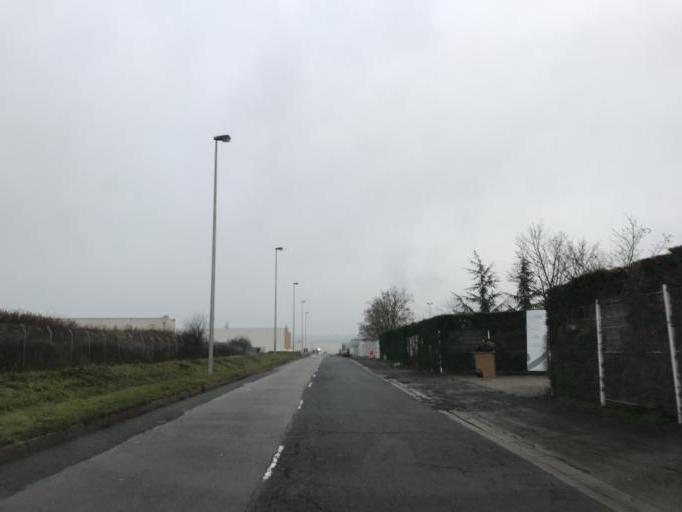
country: FR
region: Rhone-Alpes
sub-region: Departement de l'Ain
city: Jassans-Riottier
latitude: 45.9795
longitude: 4.7424
